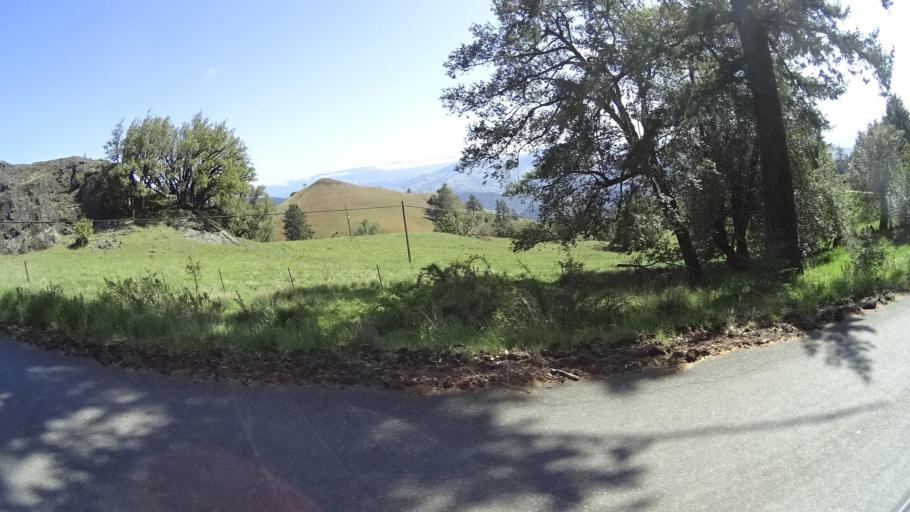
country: US
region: California
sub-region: Humboldt County
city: Redway
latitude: 40.0862
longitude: -123.6721
